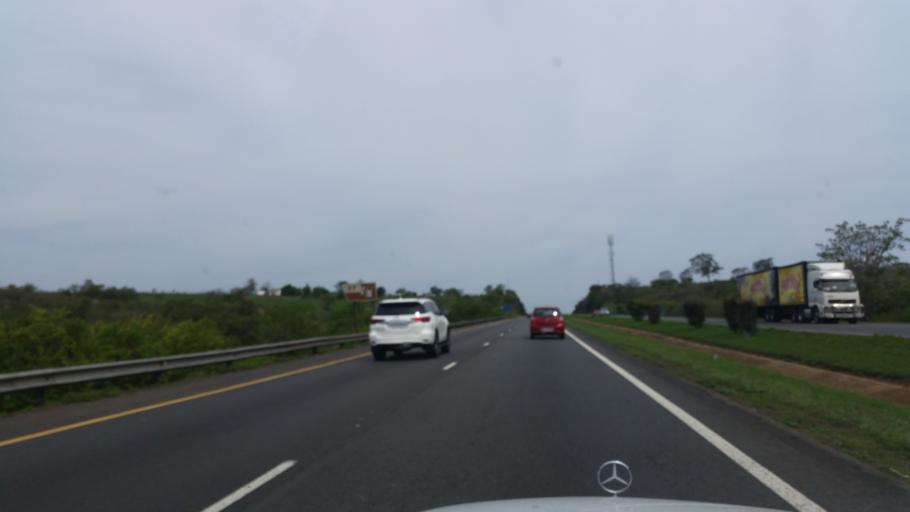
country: ZA
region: KwaZulu-Natal
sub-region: uMgungundlovu District Municipality
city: Pietermaritzburg
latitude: -29.6550
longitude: 30.4513
